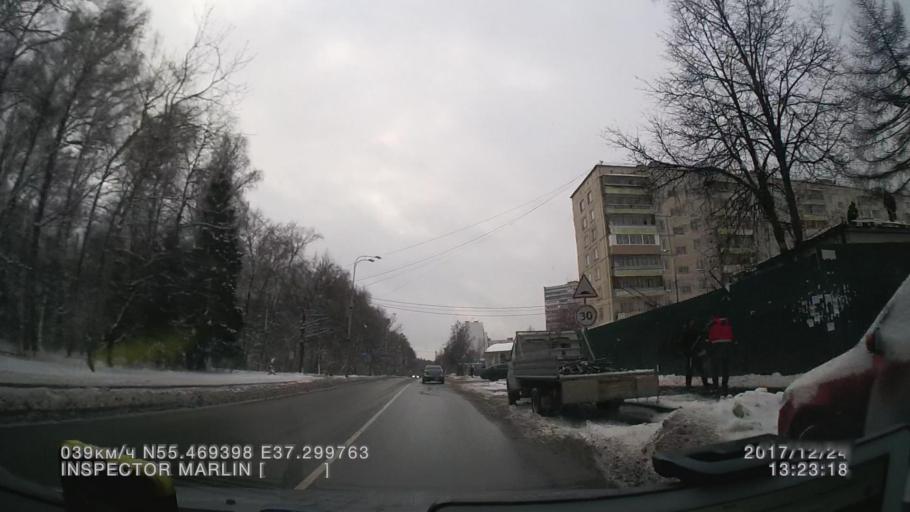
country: RU
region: Moskovskaya
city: Troitsk
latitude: 55.4693
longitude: 37.2996
